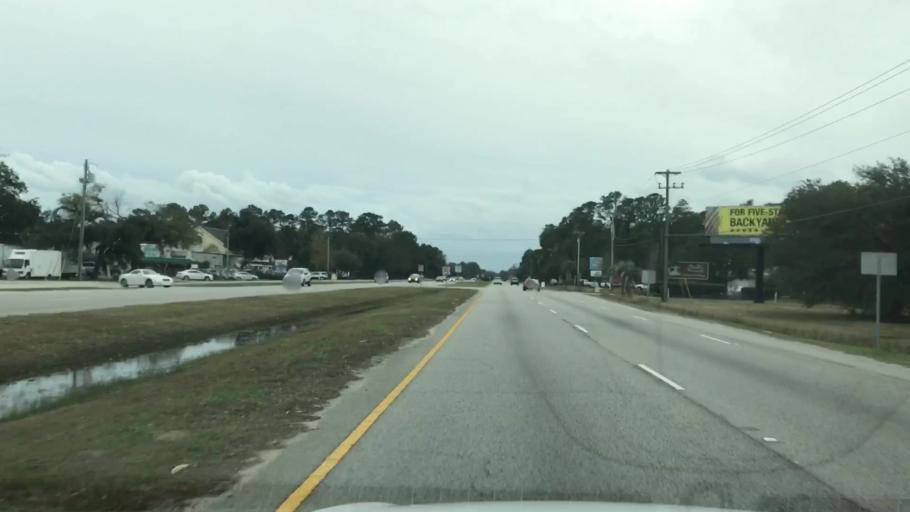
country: US
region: South Carolina
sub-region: Georgetown County
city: Murrells Inlet
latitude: 33.5429
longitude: -79.0531
